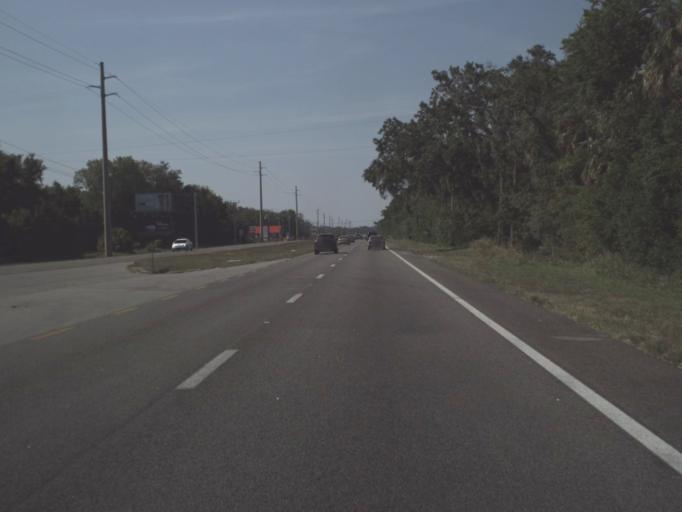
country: US
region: Florida
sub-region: Brevard County
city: Sharpes
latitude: 28.4245
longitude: -80.7576
